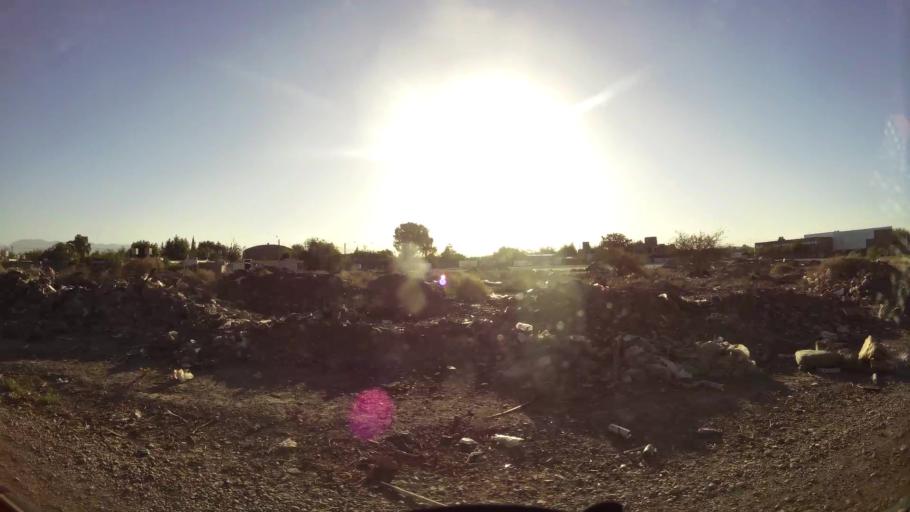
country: AR
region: San Juan
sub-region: Departamento de Santa Lucia
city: Santa Lucia
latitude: -31.5450
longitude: -68.5093
